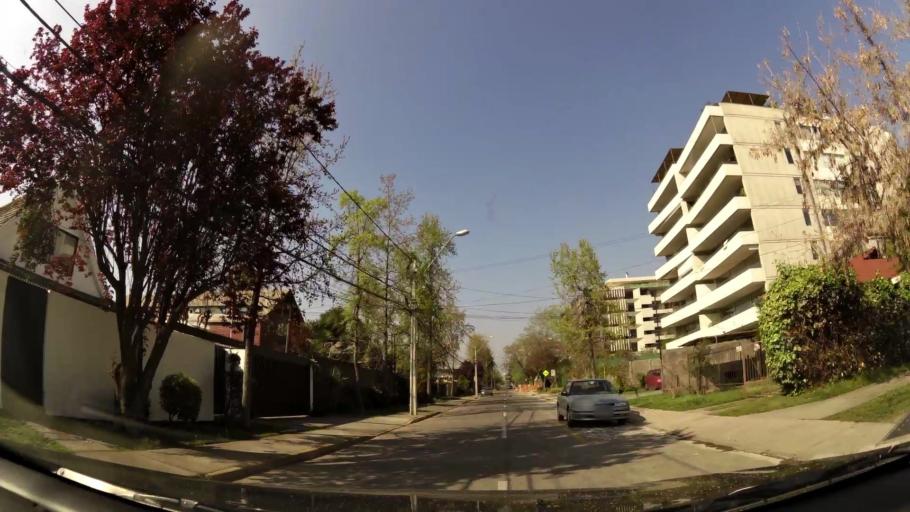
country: CL
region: Santiago Metropolitan
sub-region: Provincia de Santiago
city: Villa Presidente Frei, Nunoa, Santiago, Chile
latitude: -33.3948
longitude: -70.5653
